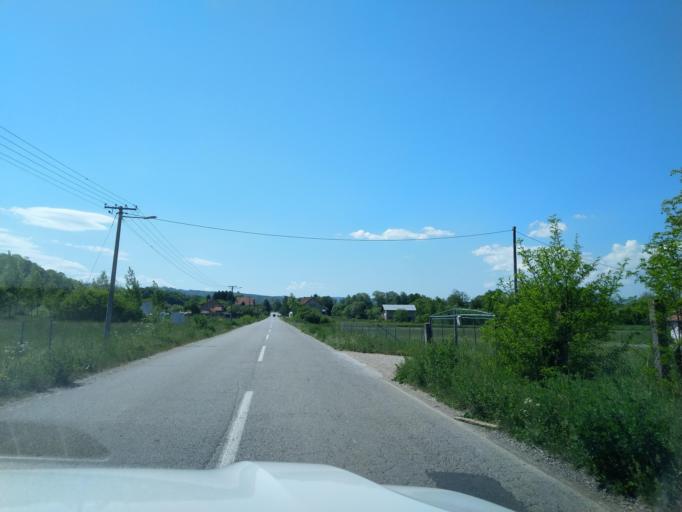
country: RS
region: Central Serbia
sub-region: Zlatiborski Okrug
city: Pozega
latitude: 43.8553
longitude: 19.9854
